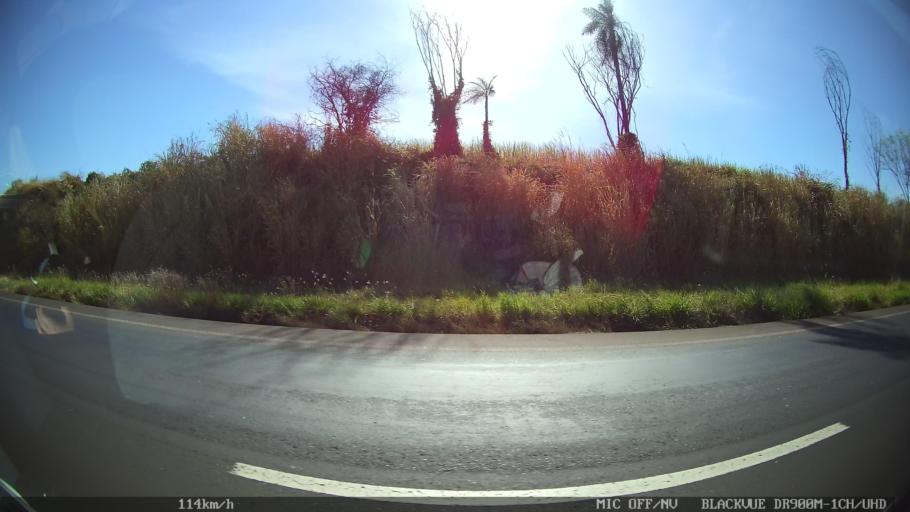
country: BR
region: Sao Paulo
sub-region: Barretos
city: Barretos
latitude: -20.5987
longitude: -48.7231
